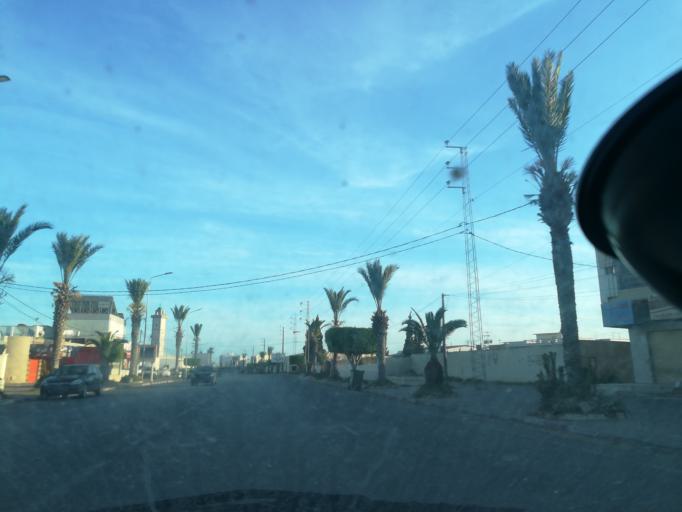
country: TN
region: Safaqis
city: Al Qarmadah
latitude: 34.8233
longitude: 10.7630
